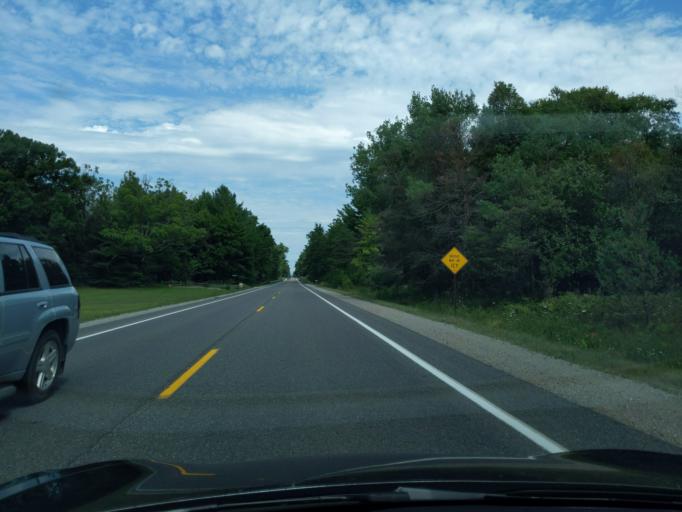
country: US
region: Michigan
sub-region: Midland County
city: Midland
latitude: 43.5920
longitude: -84.3691
